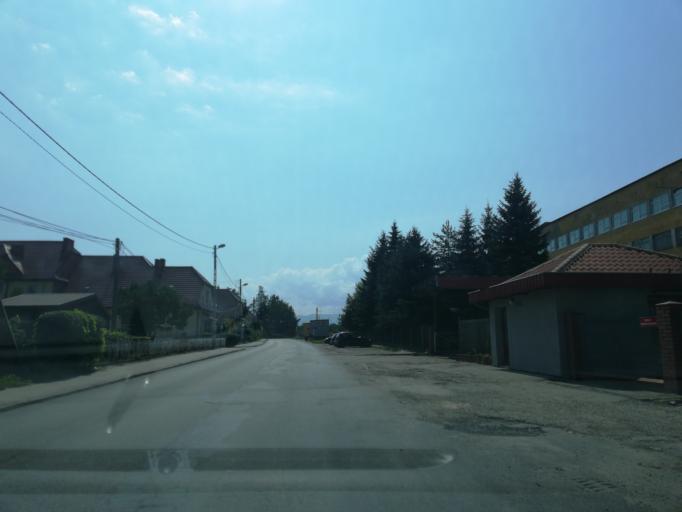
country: PL
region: Lesser Poland Voivodeship
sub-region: Powiat nowosadecki
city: Nowy Sacz
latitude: 49.6015
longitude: 20.7029
